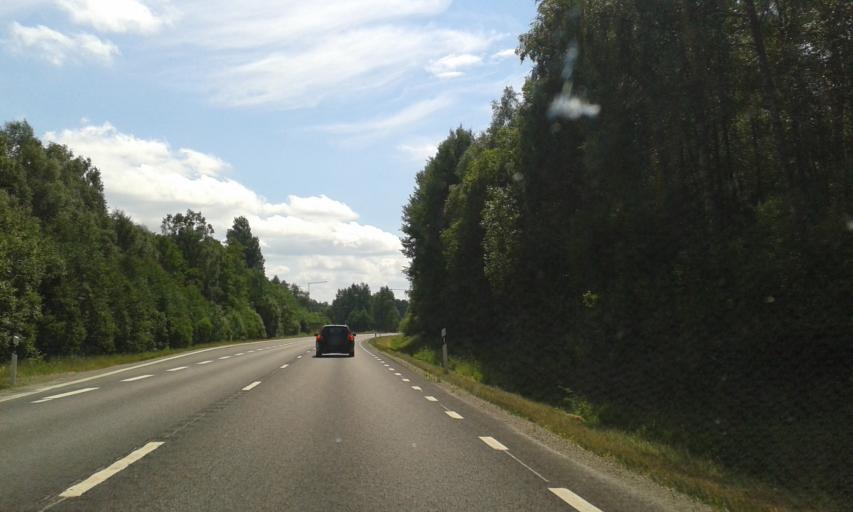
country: SE
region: Joenkoeping
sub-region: Varnamo Kommun
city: Rydaholm
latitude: 56.9894
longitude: 14.2972
